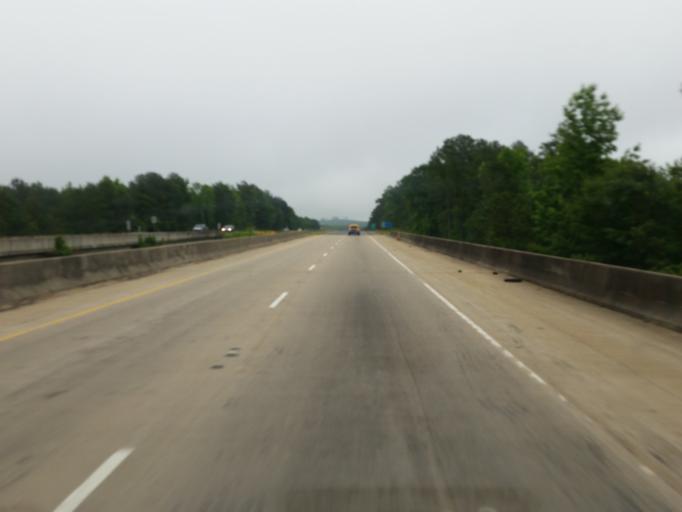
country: US
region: Louisiana
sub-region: Bienville Parish
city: Arcadia
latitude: 32.5633
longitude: -93.0642
